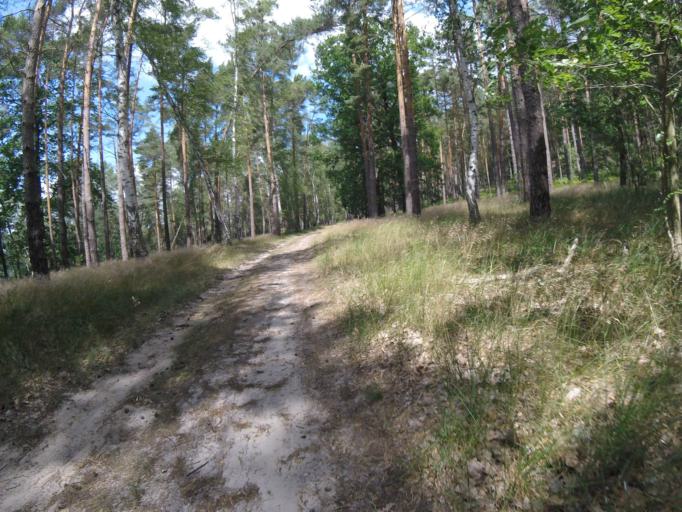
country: DE
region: Brandenburg
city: Bestensee
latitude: 52.2048
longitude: 13.6394
